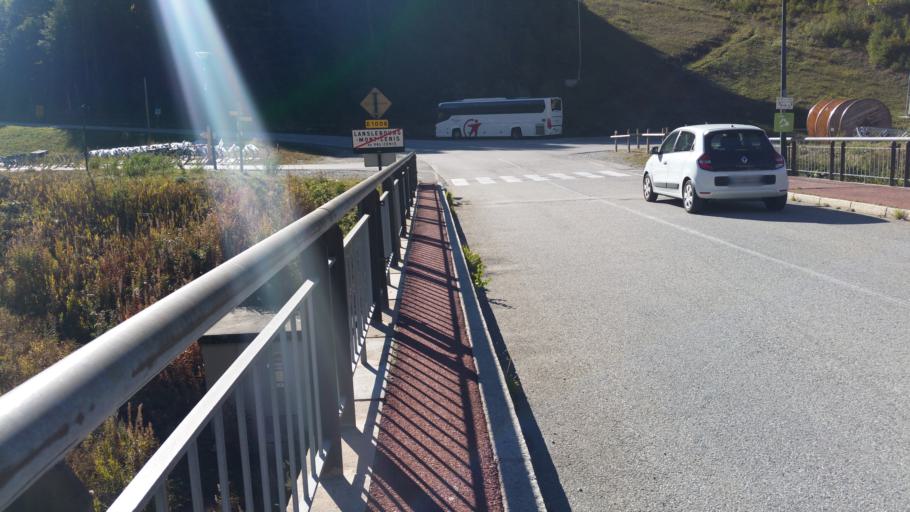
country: IT
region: Piedmont
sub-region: Provincia di Torino
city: Moncenisio
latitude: 45.2850
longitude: 6.8829
